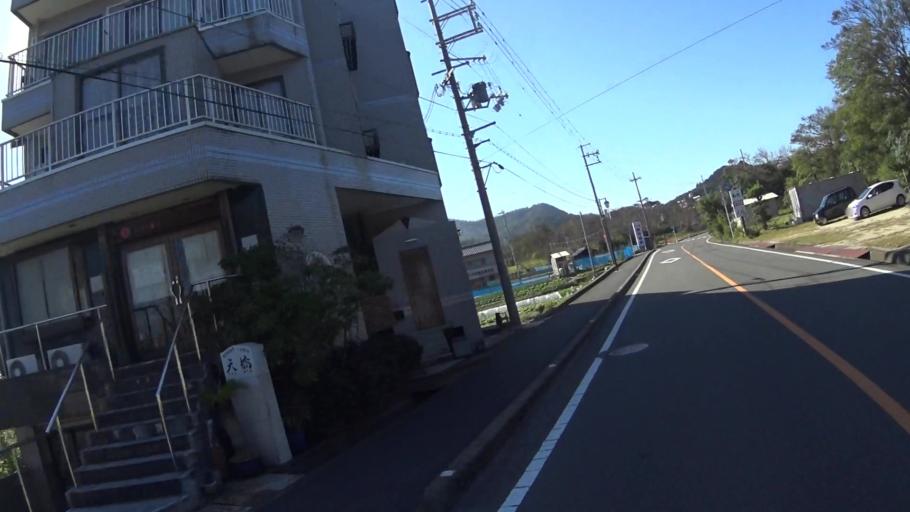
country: JP
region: Hyogo
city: Toyooka
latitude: 35.6436
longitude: 134.9084
